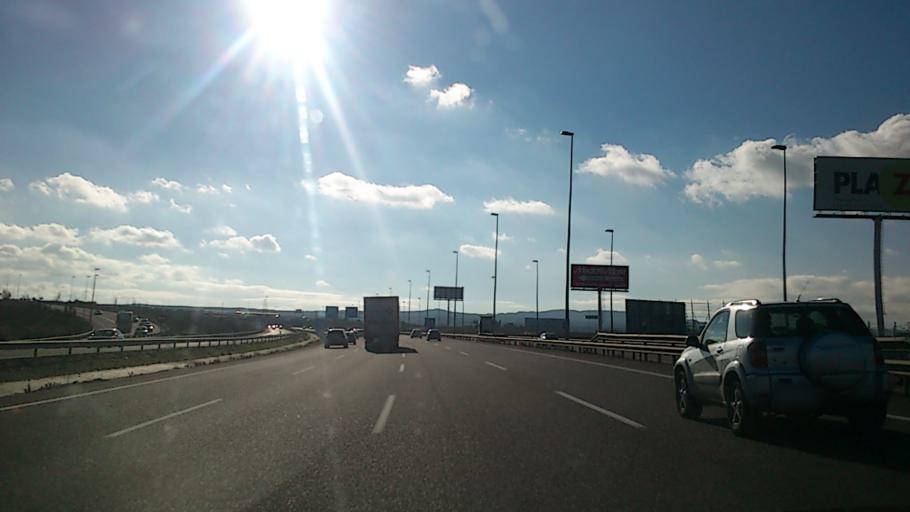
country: ES
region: Aragon
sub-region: Provincia de Zaragoza
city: Montecanal
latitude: 41.6426
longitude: -0.9706
